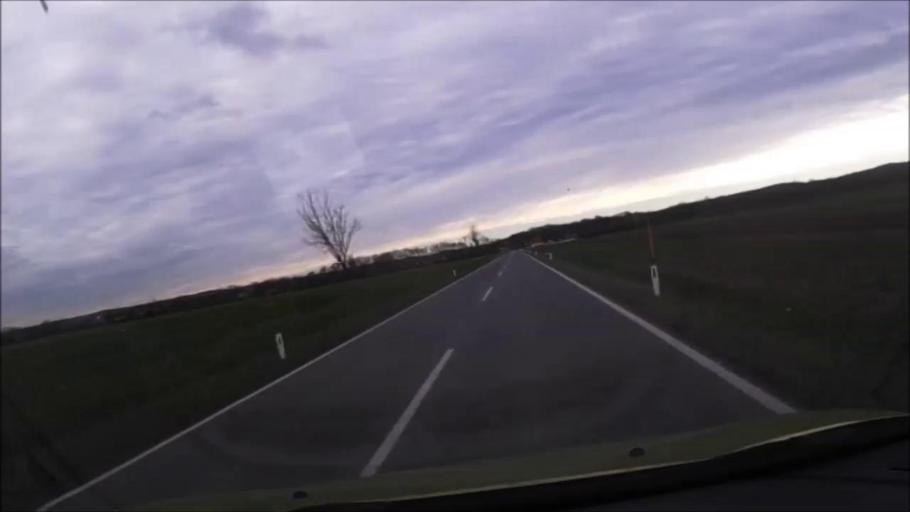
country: AT
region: Burgenland
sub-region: Eisenstadt-Umgebung
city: Leithaprodersdorf
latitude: 47.9458
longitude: 16.4604
